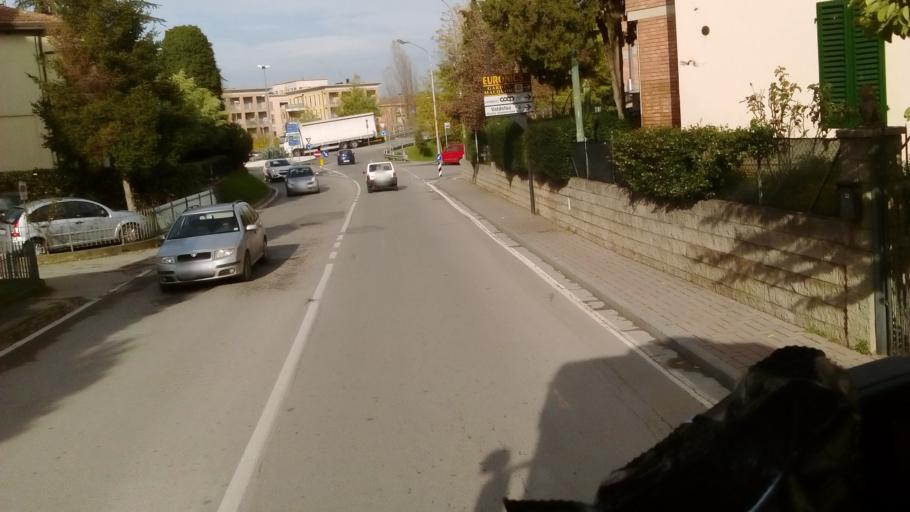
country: IT
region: Tuscany
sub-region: Provincia di Siena
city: Poggibonsi
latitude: 43.4625
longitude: 11.1576
